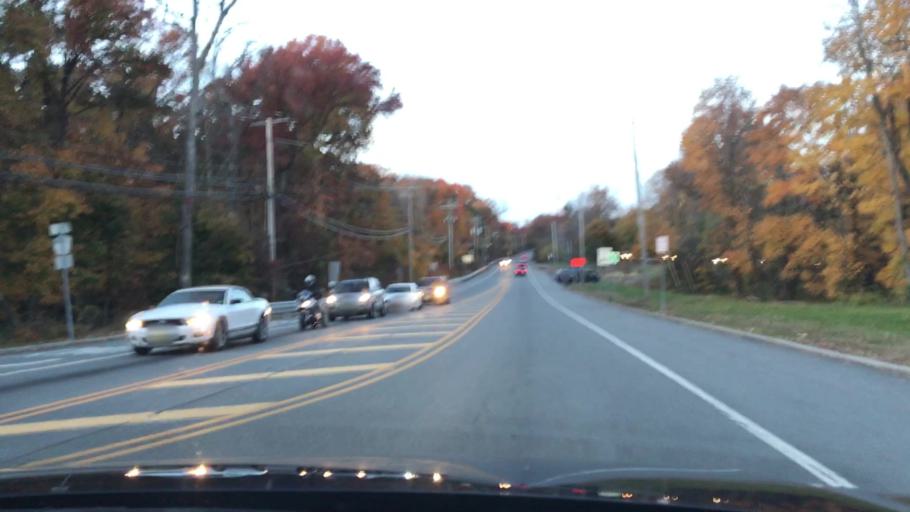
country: US
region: New Jersey
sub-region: Bergen County
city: Alpine
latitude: 40.9466
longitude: -73.9230
